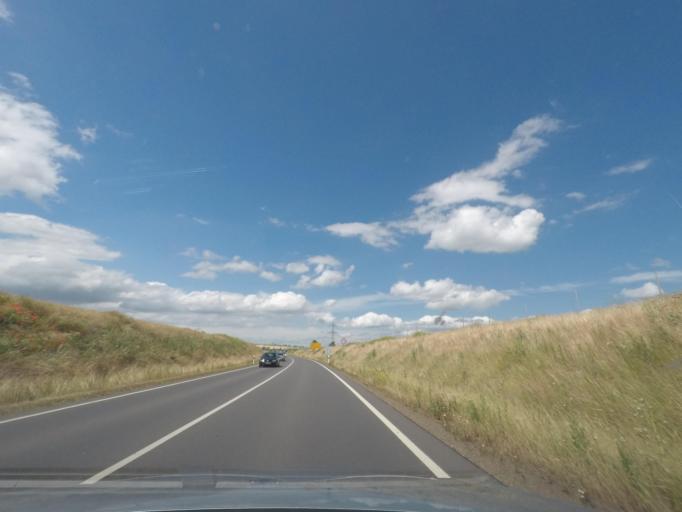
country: DE
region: Saxony-Anhalt
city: Gross Quenstedt
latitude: 51.9083
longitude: 11.1118
